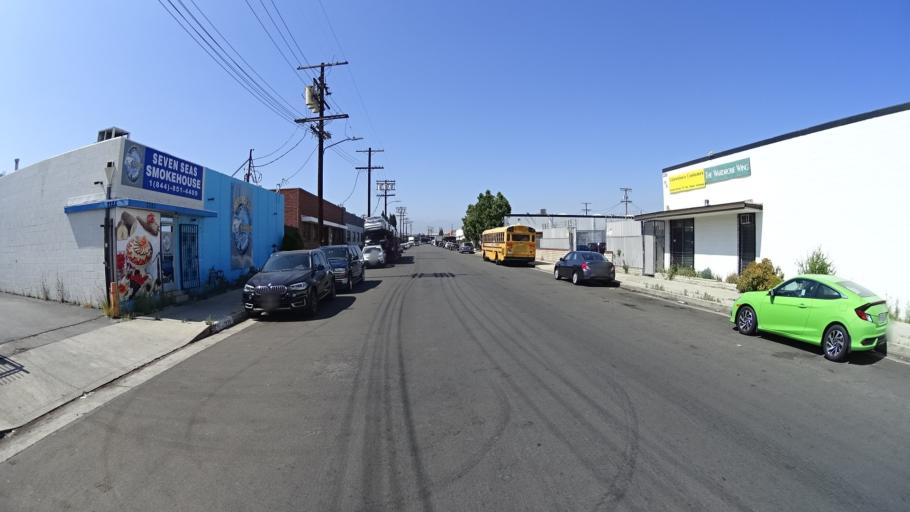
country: US
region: California
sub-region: Los Angeles County
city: Van Nuys
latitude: 34.2032
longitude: -118.4263
